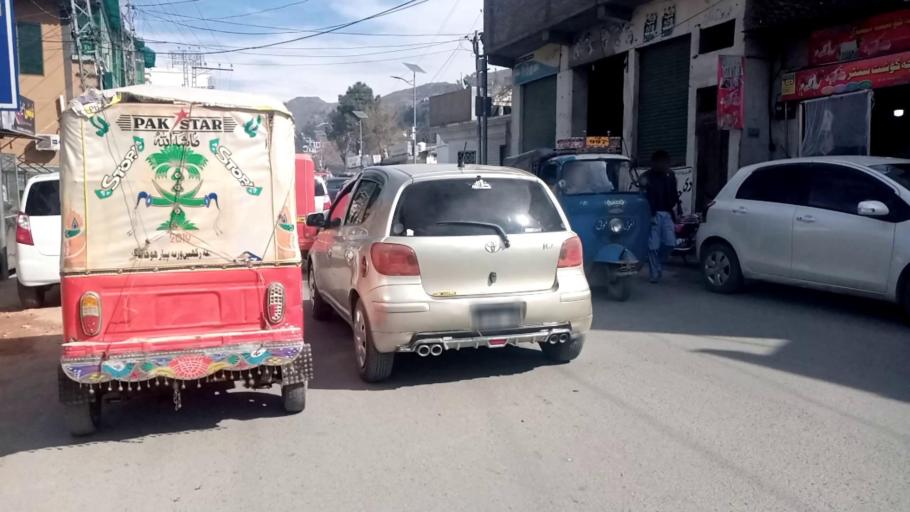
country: PK
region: Khyber Pakhtunkhwa
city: Saidu Sharif
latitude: 34.7472
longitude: 72.3552
